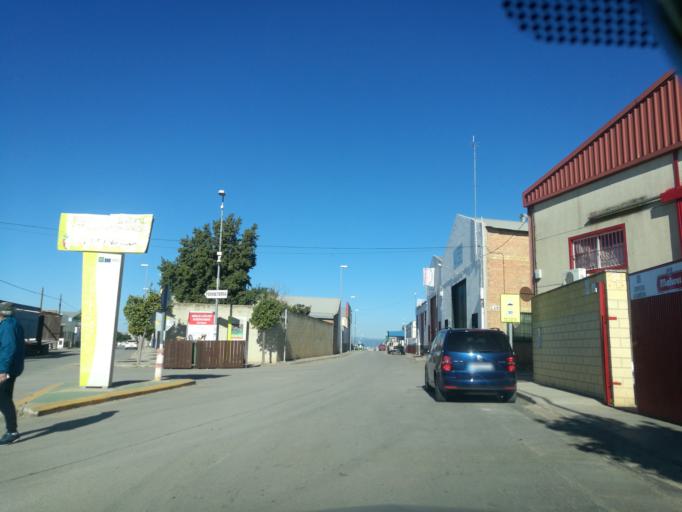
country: ES
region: Andalusia
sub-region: Provincia de Sevilla
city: La Campana
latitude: 37.5739
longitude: -5.4303
